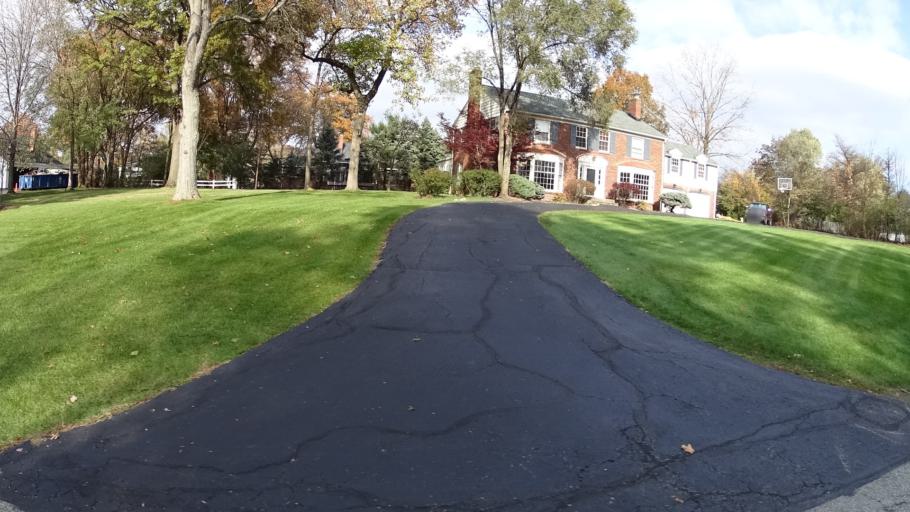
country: US
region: Ohio
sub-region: Lorain County
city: Elyria
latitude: 41.3854
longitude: -82.0959
